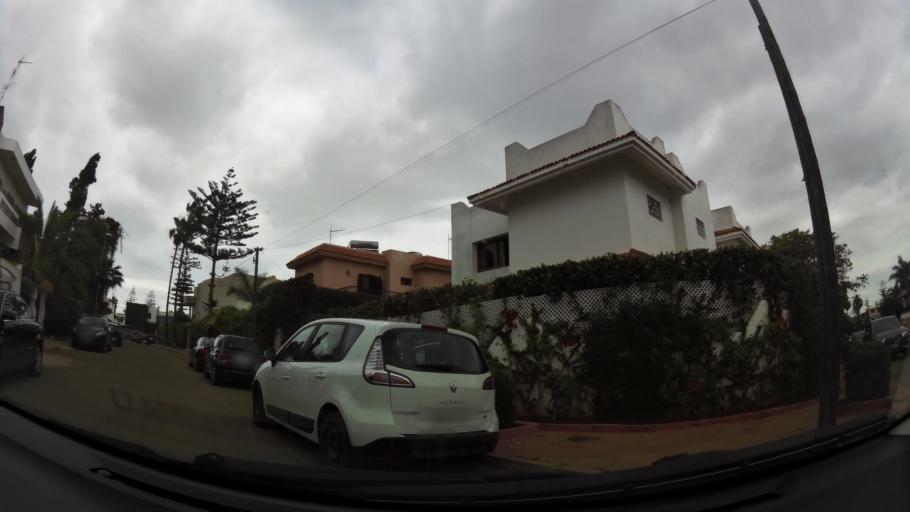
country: MA
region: Grand Casablanca
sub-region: Casablanca
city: Casablanca
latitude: 33.5696
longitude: -7.6584
